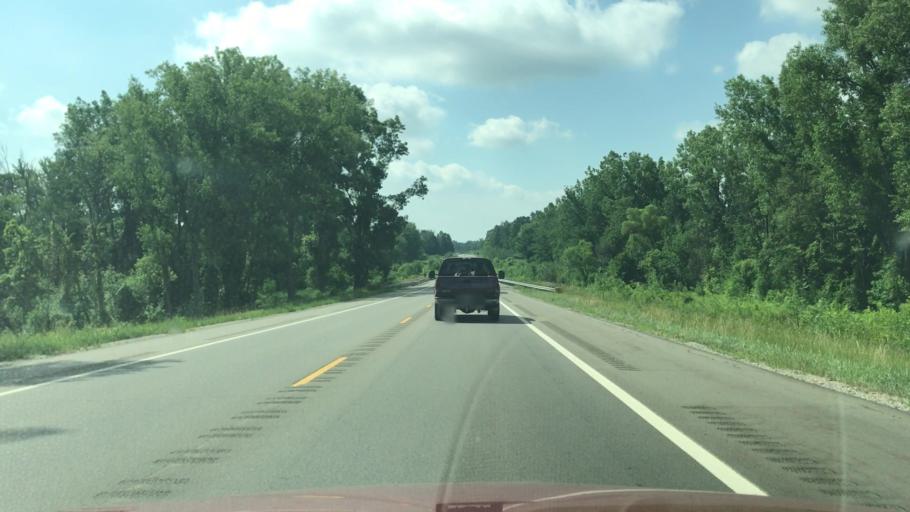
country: US
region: Michigan
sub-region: Kent County
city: Sparta
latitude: 43.1399
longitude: -85.7187
